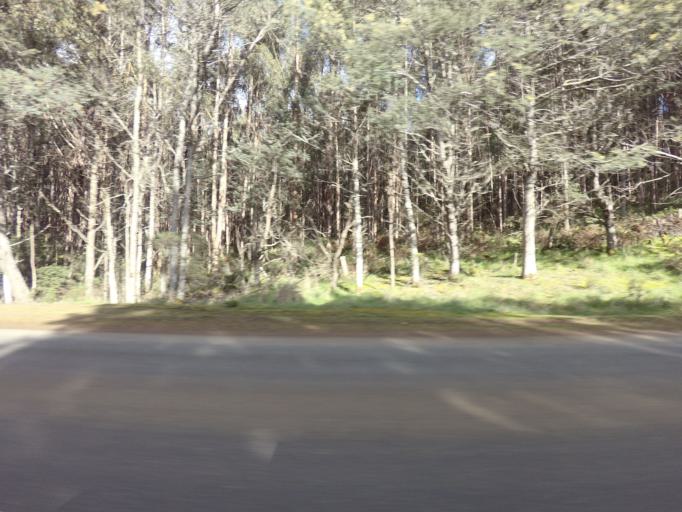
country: AU
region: Tasmania
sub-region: Huon Valley
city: Geeveston
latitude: -43.3451
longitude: 146.9616
